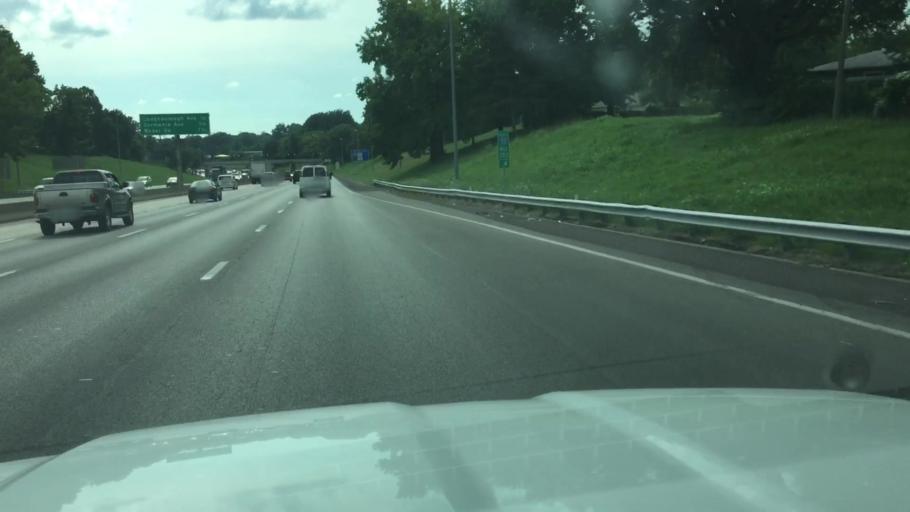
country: US
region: Missouri
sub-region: Saint Louis County
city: Lemay
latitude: 38.5617
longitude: -90.2508
